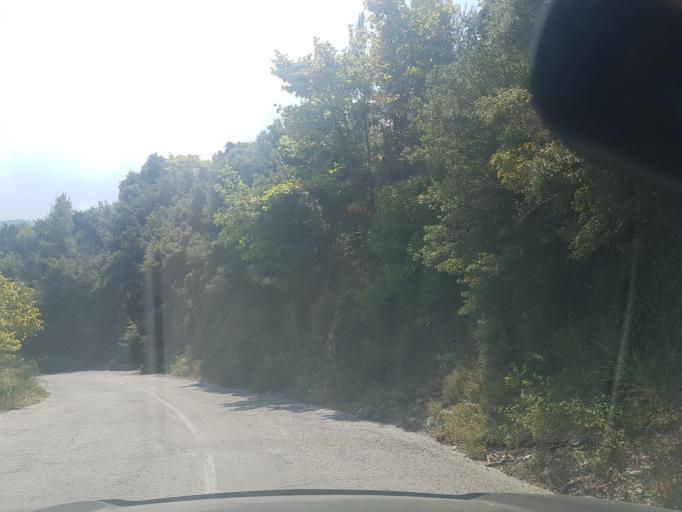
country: GR
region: Central Greece
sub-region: Nomos Evvoias
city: Kymi
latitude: 38.6503
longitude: 23.9025
